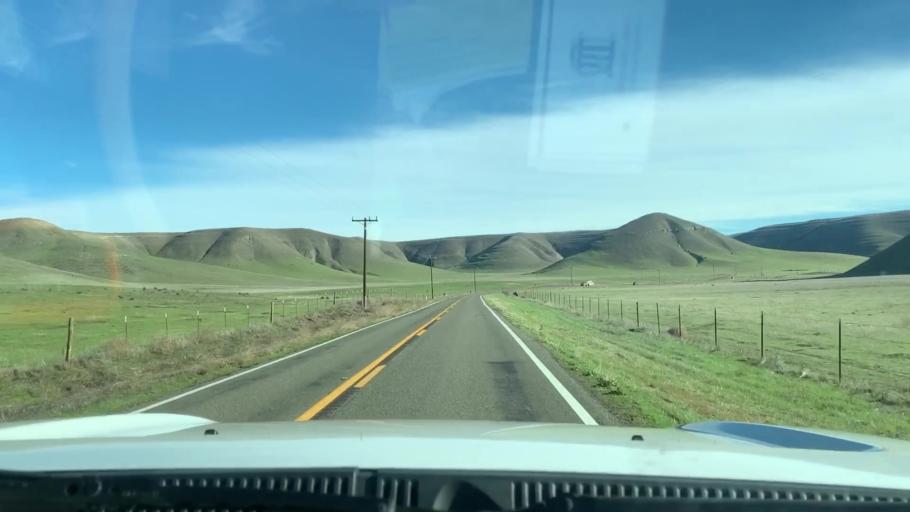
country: US
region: California
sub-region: Monterey County
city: King City
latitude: 36.1559
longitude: -120.9926
